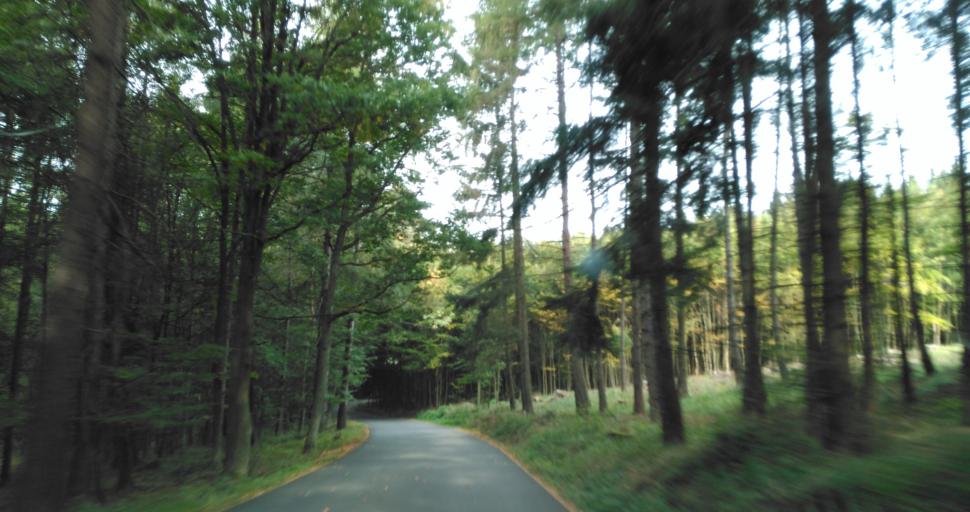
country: CZ
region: Plzensky
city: Zbiroh
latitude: 49.9294
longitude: 13.7903
